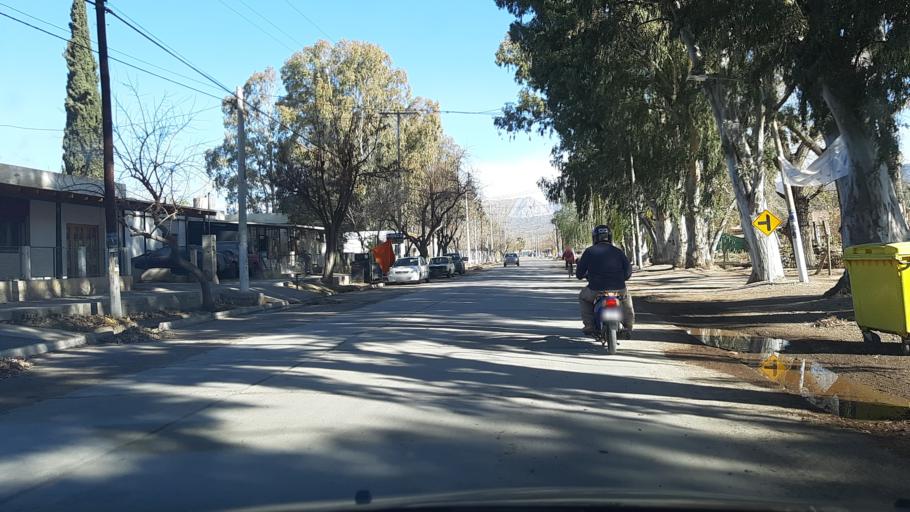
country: AR
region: San Juan
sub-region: Departamento de Zonda
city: Zonda
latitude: -31.4617
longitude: -68.7373
